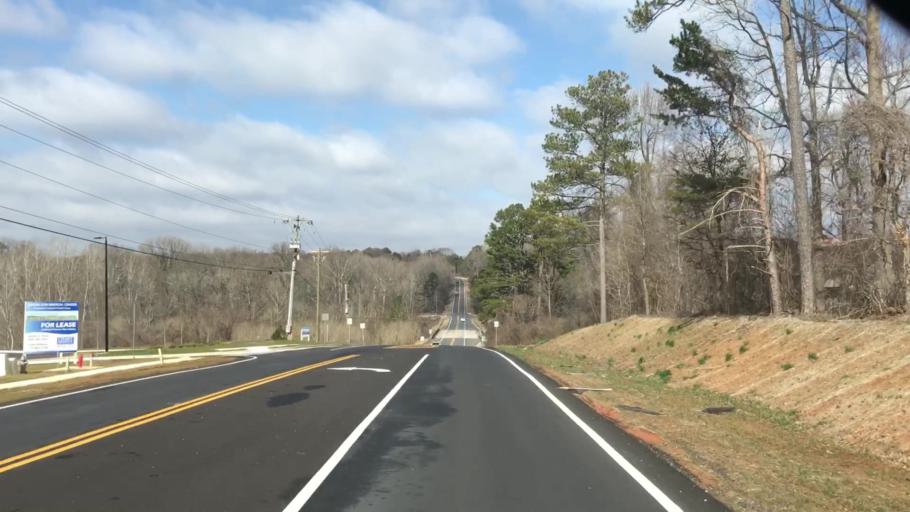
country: US
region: Georgia
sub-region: Jackson County
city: Braselton
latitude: 34.1270
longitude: -83.8301
